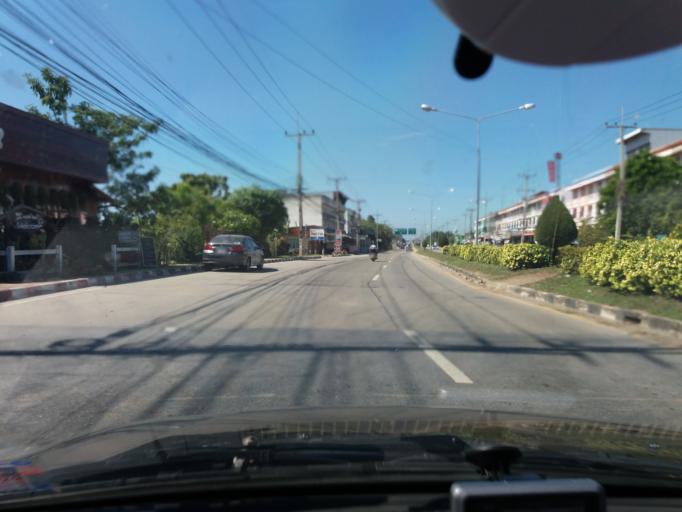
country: TH
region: Suphan Buri
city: Suphan Buri
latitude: 14.4616
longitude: 100.1496
